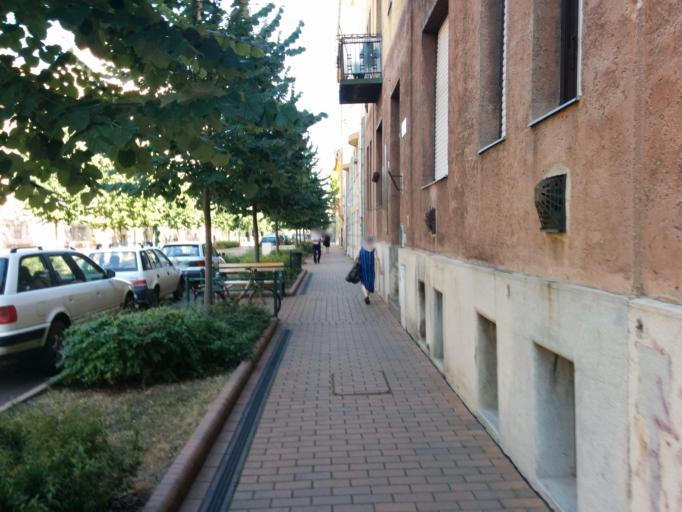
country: HU
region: Csongrad
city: Szeged
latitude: 46.2541
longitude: 20.1409
